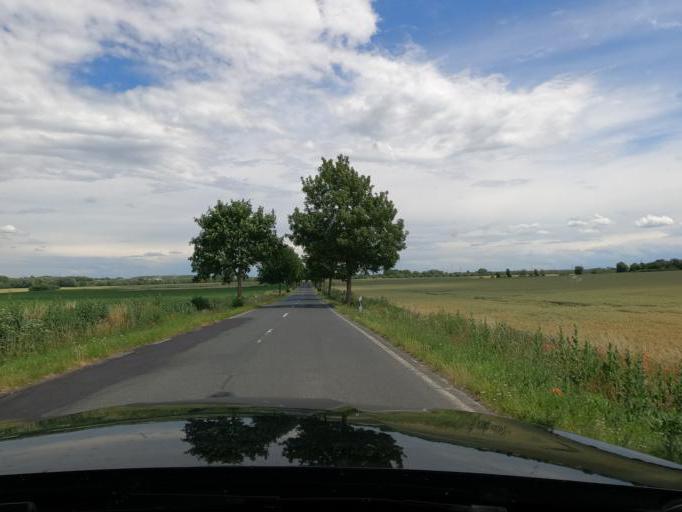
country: DE
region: Lower Saxony
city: Lengede
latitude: 52.1887
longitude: 10.2996
